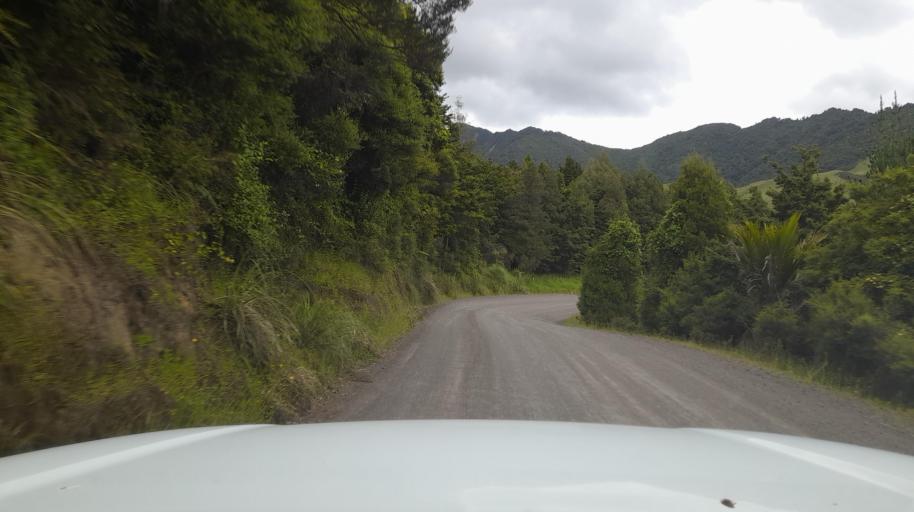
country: NZ
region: Northland
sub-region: Far North District
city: Kaitaia
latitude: -35.3256
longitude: 173.3529
